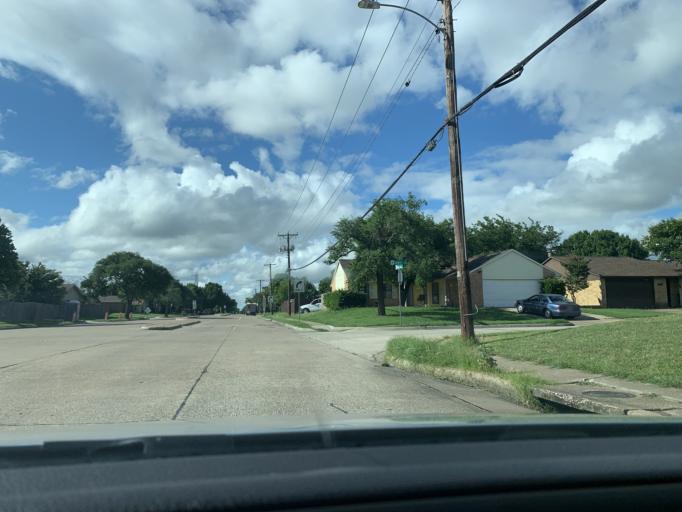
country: US
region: Texas
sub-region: Dallas County
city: Cedar Hill
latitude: 32.6523
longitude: -97.0278
